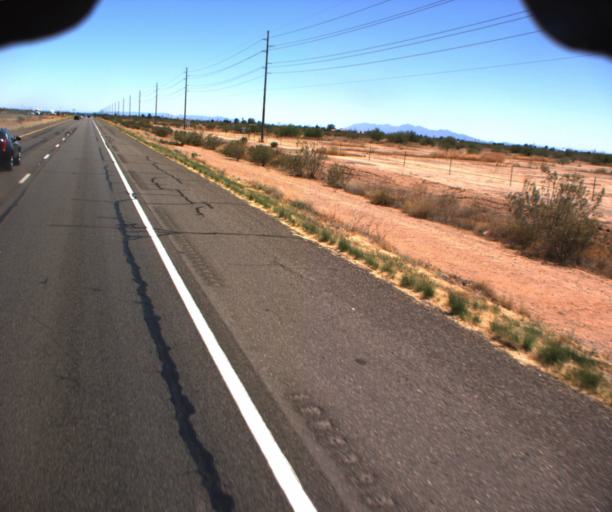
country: US
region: Arizona
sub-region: Maricopa County
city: Sun City West
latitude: 33.7202
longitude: -112.4550
